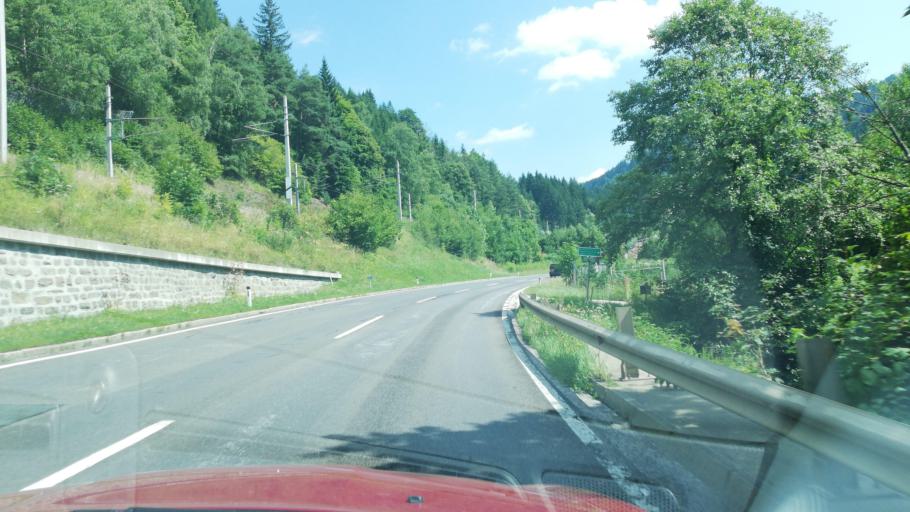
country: AT
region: Styria
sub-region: Politischer Bezirk Murau
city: Durnstein in der Steiermark
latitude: 47.0083
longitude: 14.4001
